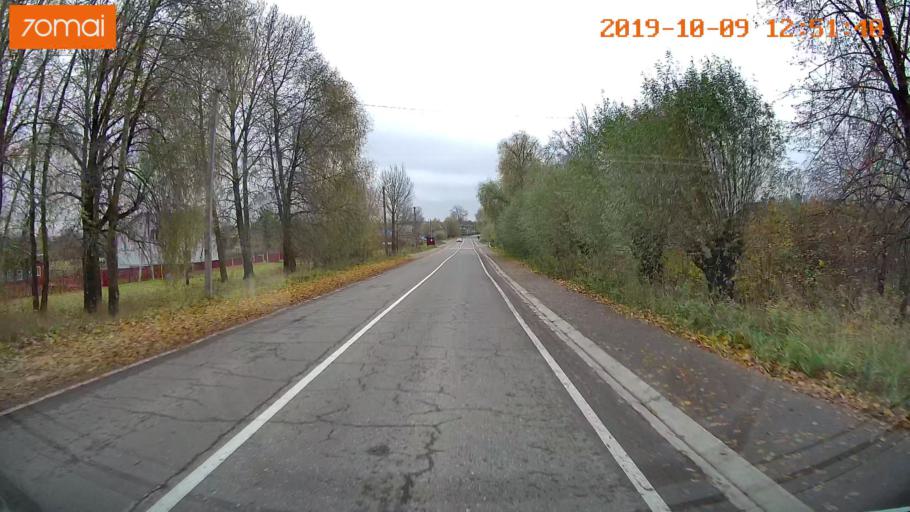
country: RU
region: Jaroslavl
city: Prechistoye
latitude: 58.4183
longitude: 40.3448
